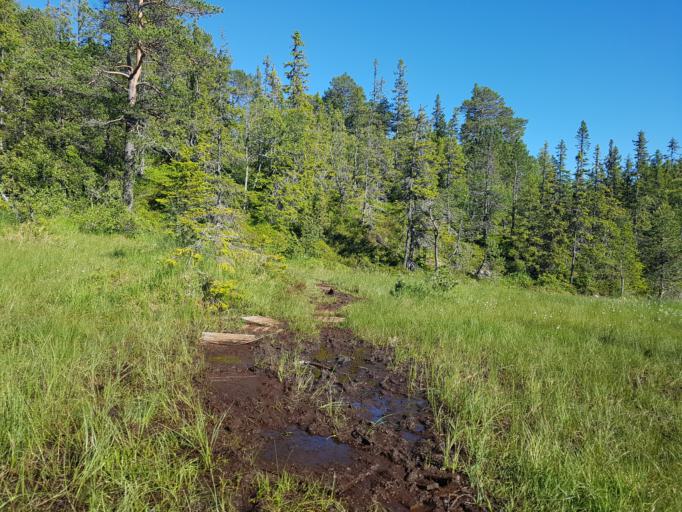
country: NO
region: Sor-Trondelag
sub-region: Trondheim
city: Trondheim
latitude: 63.4376
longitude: 10.2708
